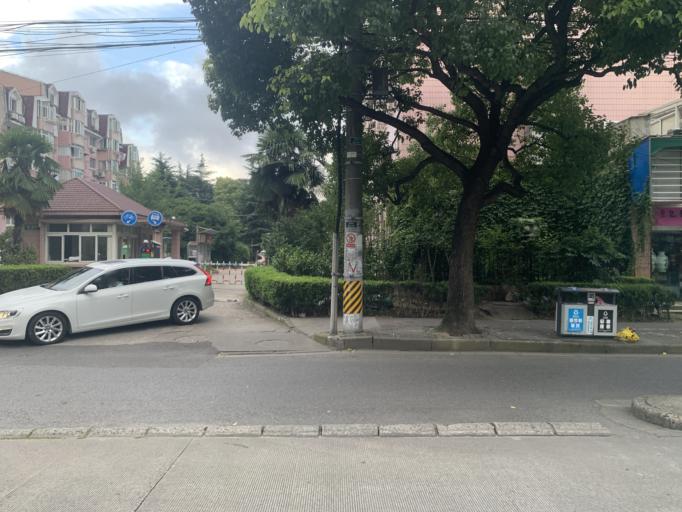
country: CN
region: Shanghai Shi
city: Pudong
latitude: 31.2516
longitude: 121.5777
